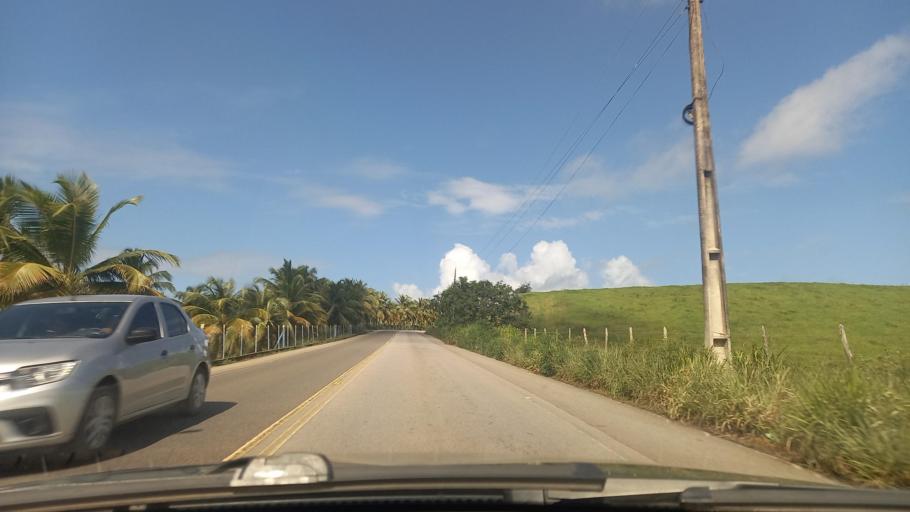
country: BR
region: Alagoas
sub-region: Marechal Deodoro
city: Marechal Deodoro
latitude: -9.8617
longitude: -35.9175
